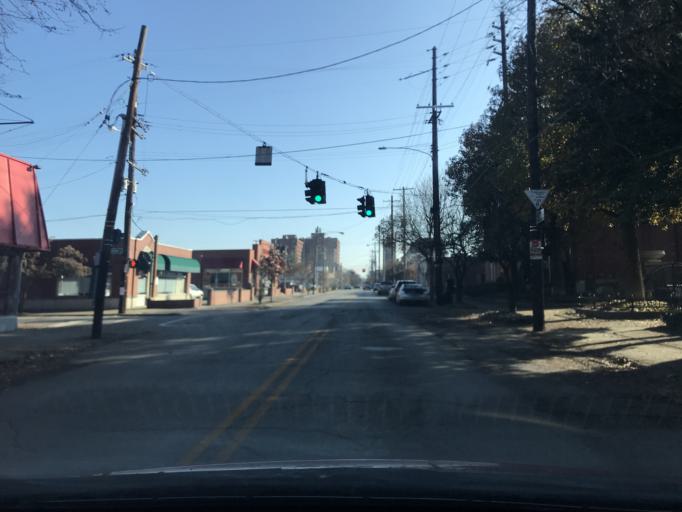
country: US
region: Kentucky
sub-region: Jefferson County
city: Louisville
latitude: 38.2351
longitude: -85.7623
